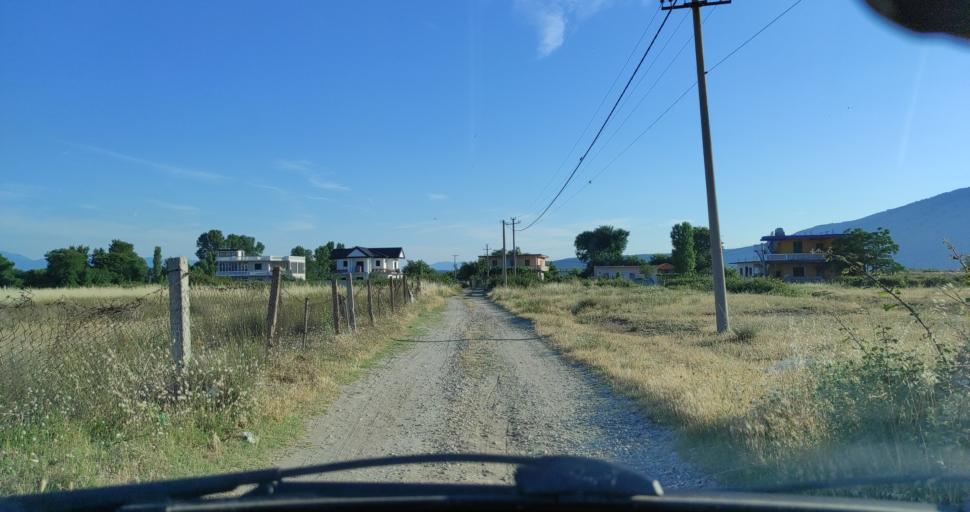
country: AL
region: Shkoder
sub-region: Rrethi i Shkodres
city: Velipoje
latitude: 41.8680
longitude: 19.4355
